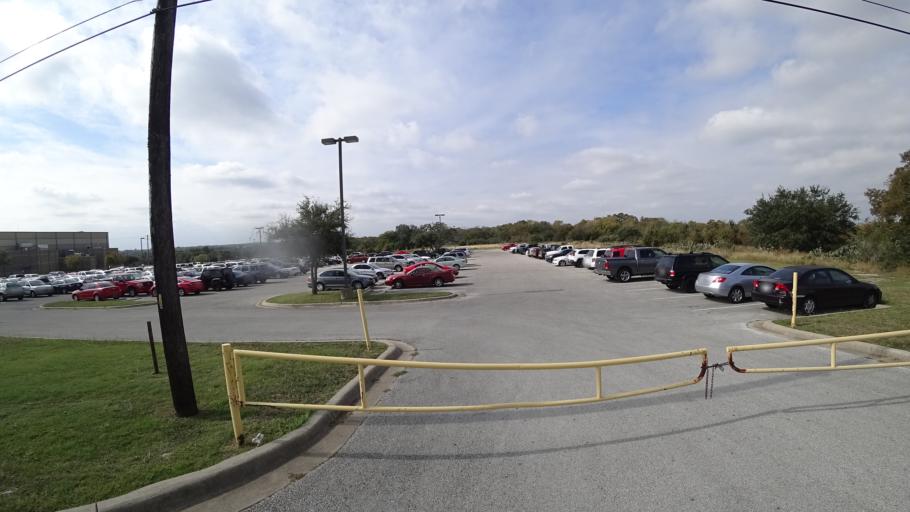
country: US
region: Texas
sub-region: Williamson County
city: Jollyville
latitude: 30.4495
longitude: -97.7356
